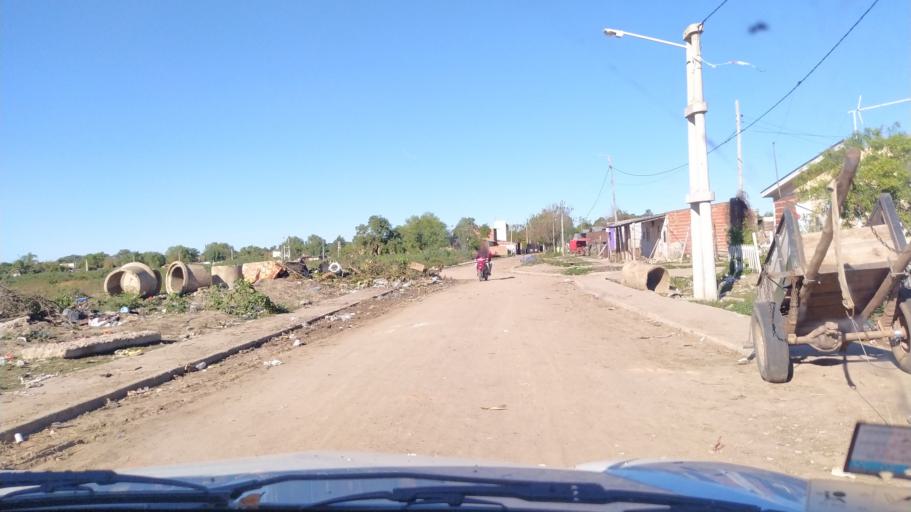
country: AR
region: Corrientes
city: Corrientes
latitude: -27.4971
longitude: -58.8036
